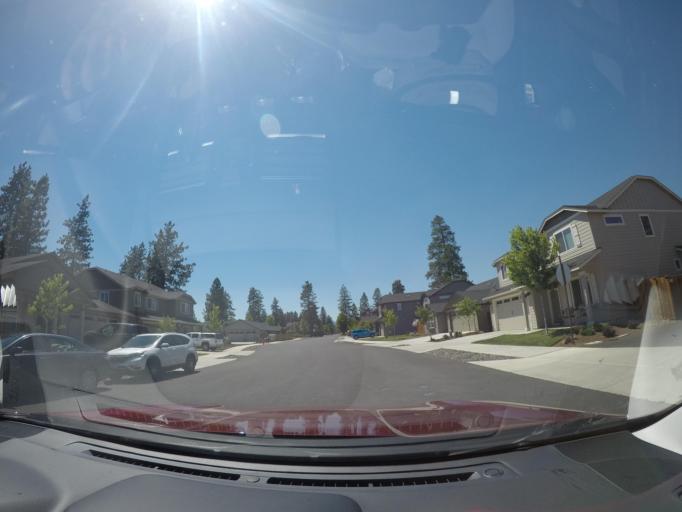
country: US
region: Oregon
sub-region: Deschutes County
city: Sisters
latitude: 44.2962
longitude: -121.5655
